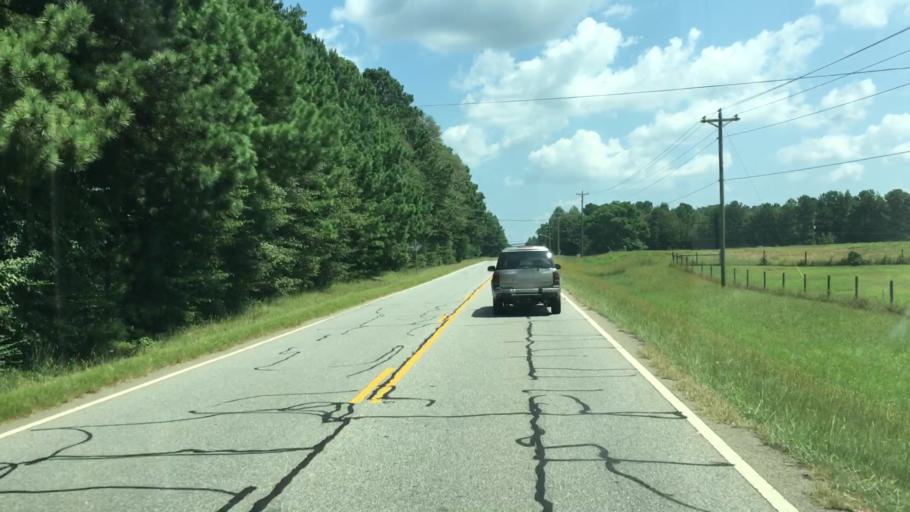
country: US
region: Georgia
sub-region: Barrow County
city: Statham
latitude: 33.9116
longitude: -83.5960
